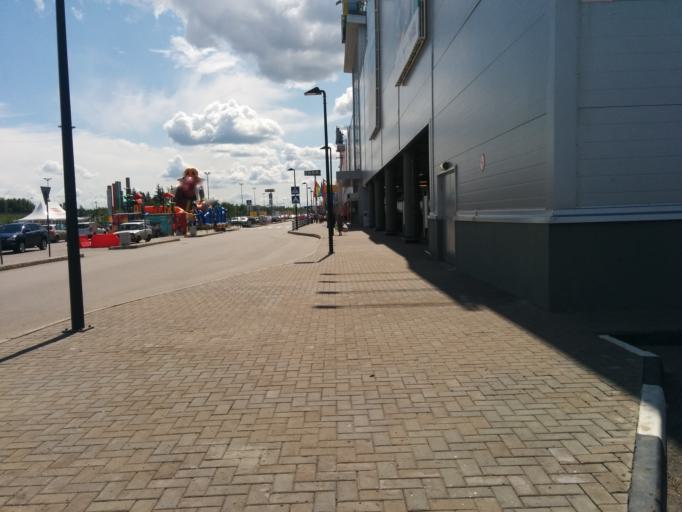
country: RU
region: Bashkortostan
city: Ufa
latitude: 54.6767
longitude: 55.9309
